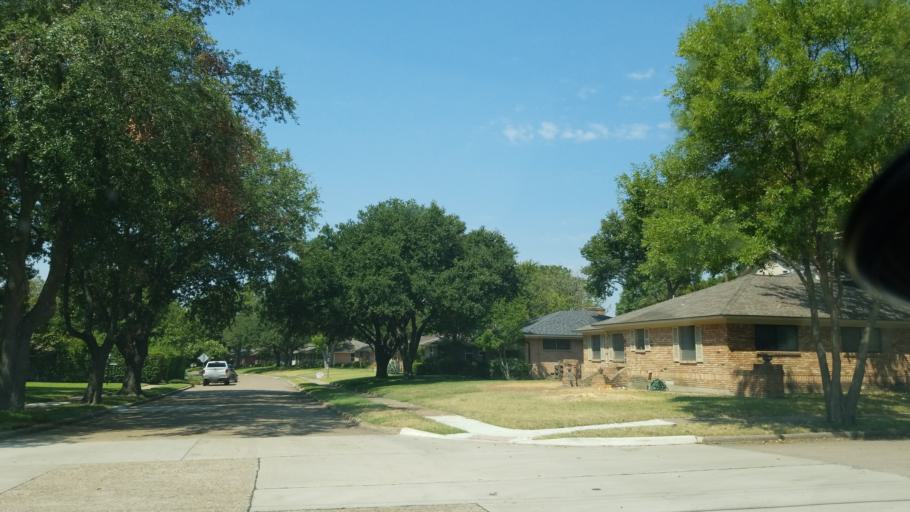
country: US
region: Texas
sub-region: Dallas County
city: Richardson
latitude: 32.8743
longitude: -96.7126
